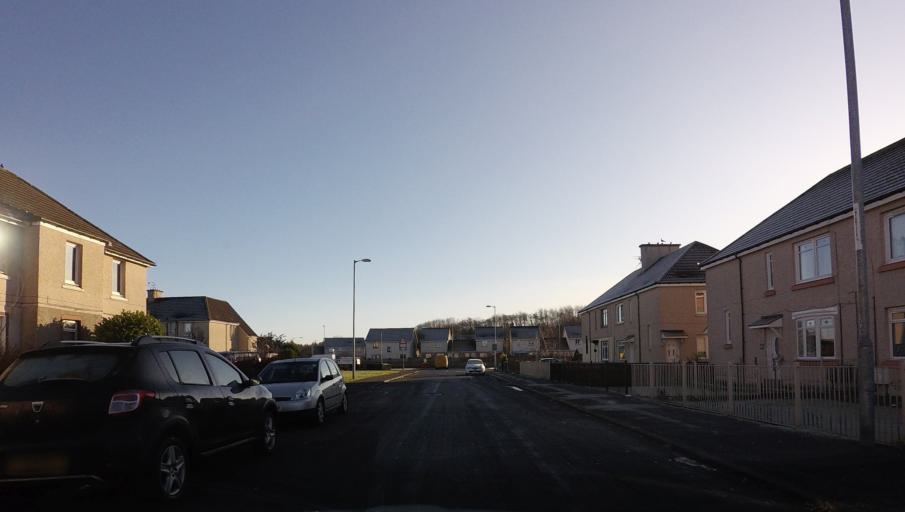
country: GB
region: Scotland
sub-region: North Lanarkshire
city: Newmains
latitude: 55.7869
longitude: -3.8718
